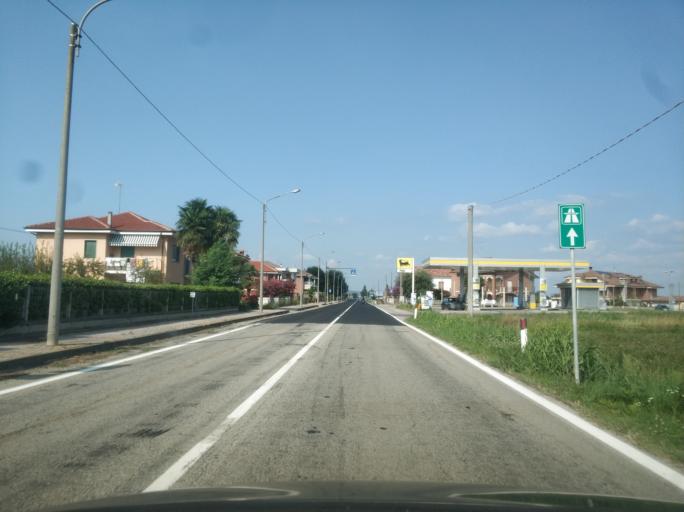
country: IT
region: Piedmont
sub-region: Provincia di Cuneo
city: Cervere
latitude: 44.6383
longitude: 7.7914
